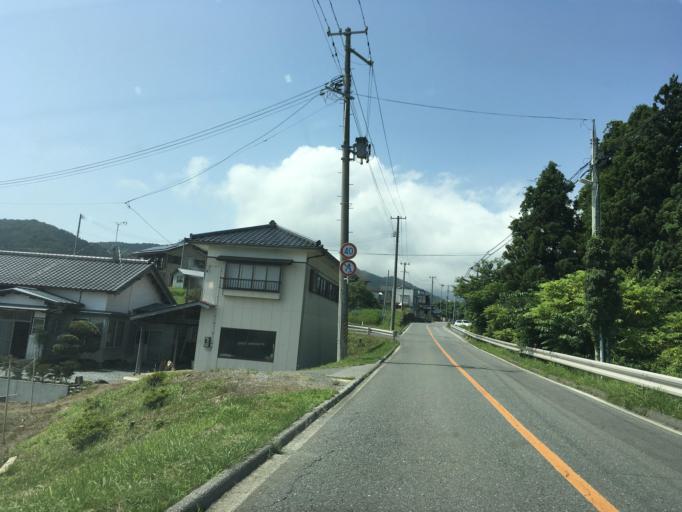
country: JP
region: Iwate
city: Ofunato
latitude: 39.0000
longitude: 141.7175
